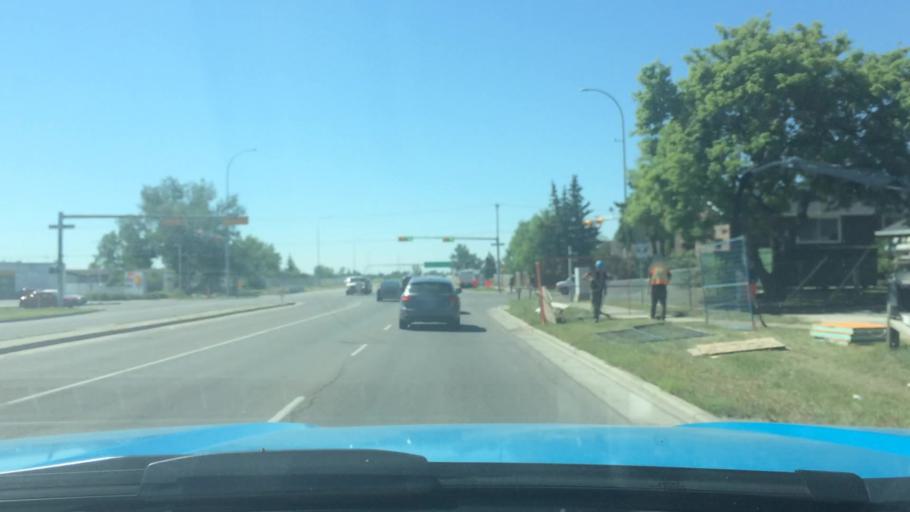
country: CA
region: Alberta
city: Calgary
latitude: 51.0723
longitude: -113.9585
